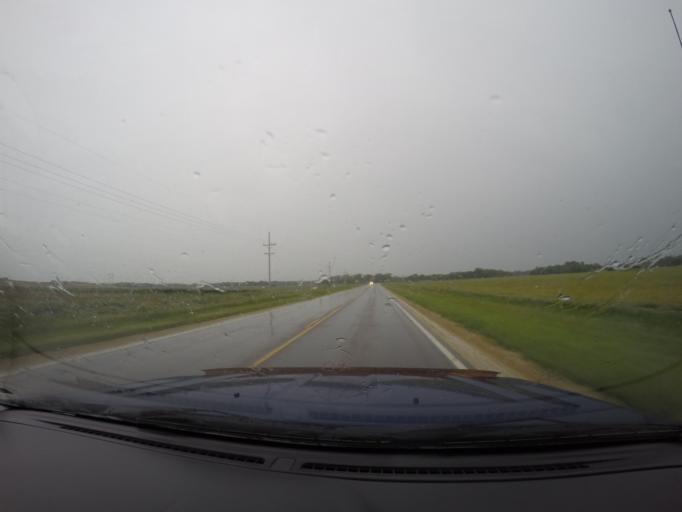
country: US
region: Kansas
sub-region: Cloud County
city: Concordia
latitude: 39.5738
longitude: -97.7009
